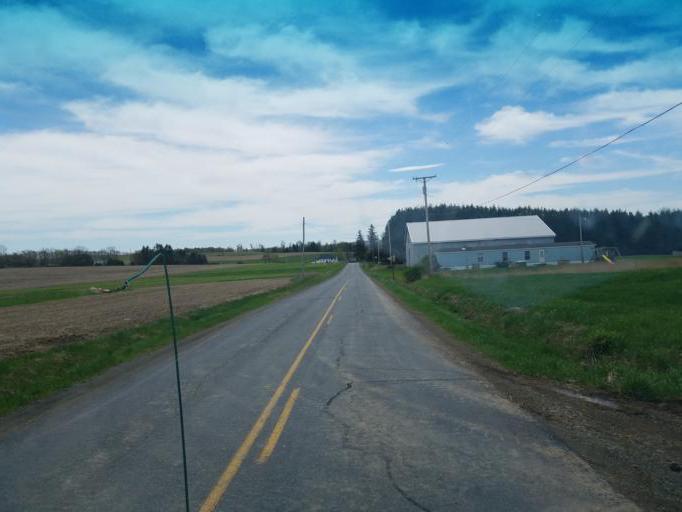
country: US
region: Pennsylvania
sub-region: Tioga County
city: Wellsboro
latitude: 41.7240
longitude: -77.3856
